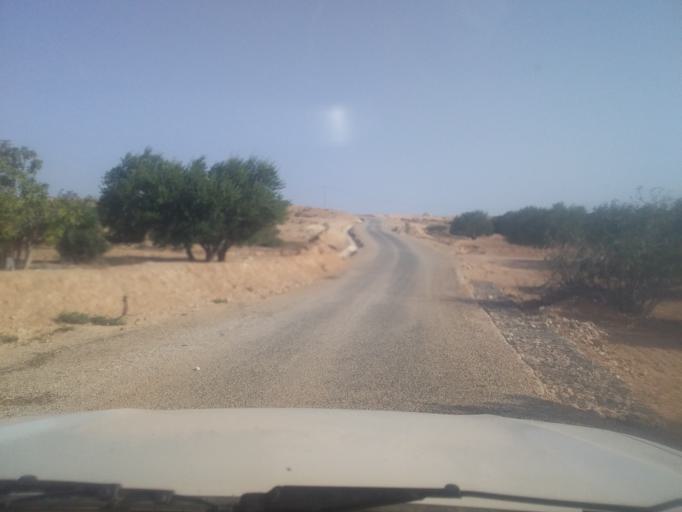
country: TN
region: Qabis
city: Matmata
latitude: 33.5843
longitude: 10.2594
